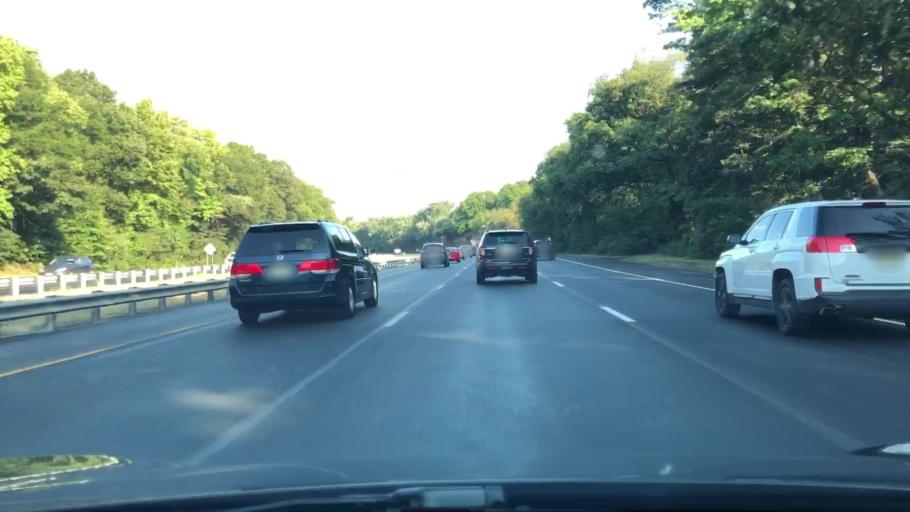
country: US
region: New Jersey
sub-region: Camden County
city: Haddon Heights
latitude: 39.8719
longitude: -75.0719
